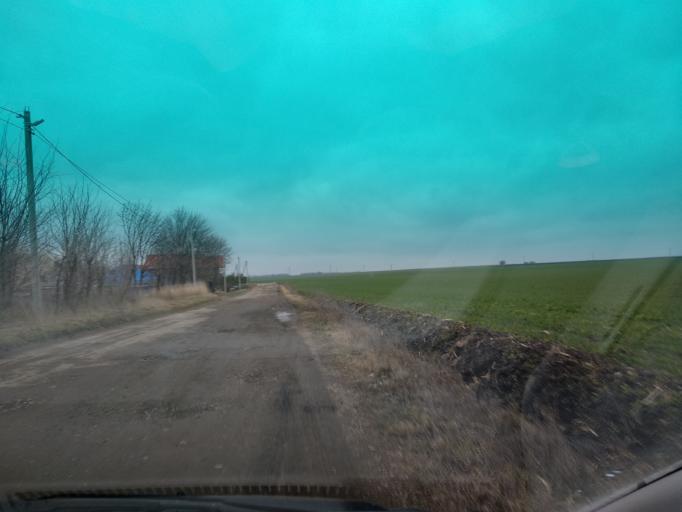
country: RU
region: Krasnodarskiy
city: Vyselki
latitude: 45.6633
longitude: 39.7021
